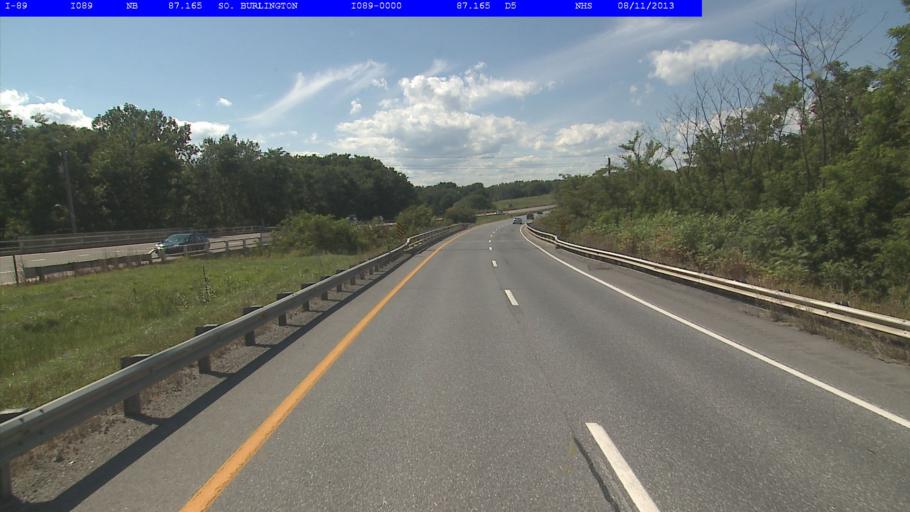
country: US
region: Vermont
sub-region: Chittenden County
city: South Burlington
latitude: 44.4496
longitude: -73.1774
